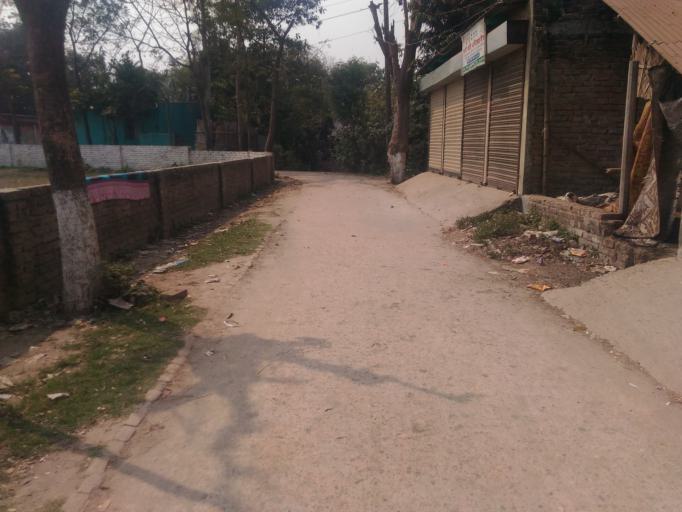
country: BD
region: Dhaka
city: Narayanganj
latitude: 23.6391
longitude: 90.4372
